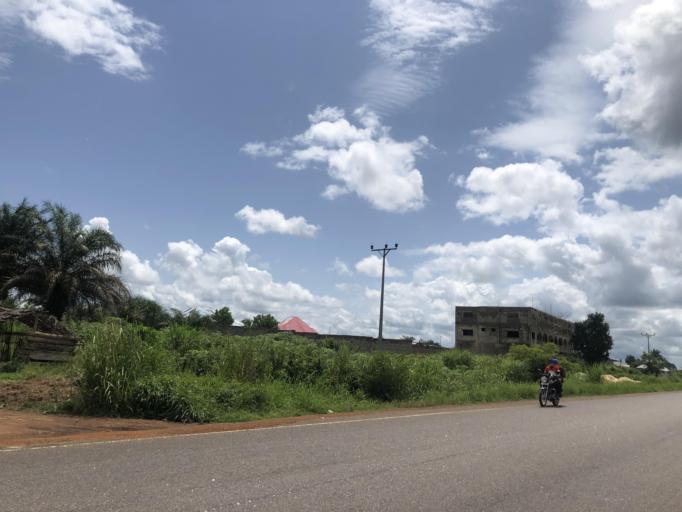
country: SL
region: Northern Province
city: Magburaka
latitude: 8.7006
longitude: -11.9239
